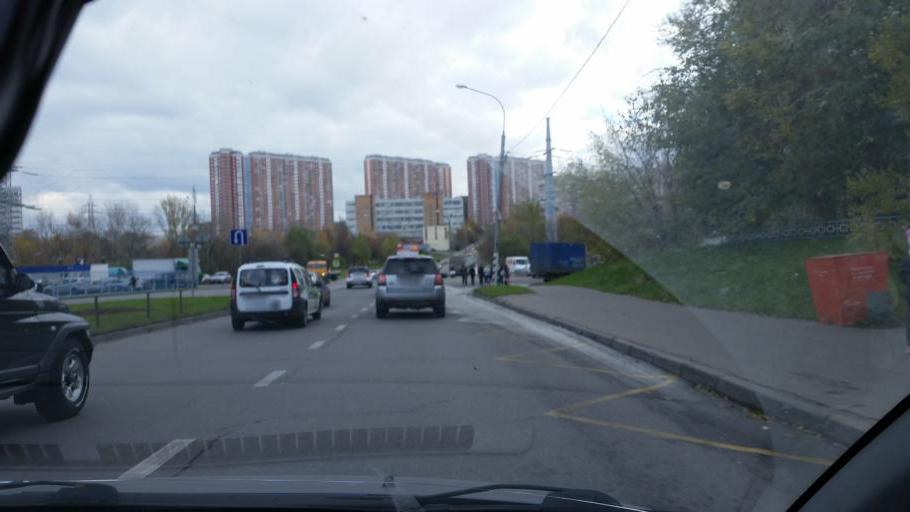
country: RU
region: Moscow
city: Kotlovka
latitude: 55.6753
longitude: 37.6030
